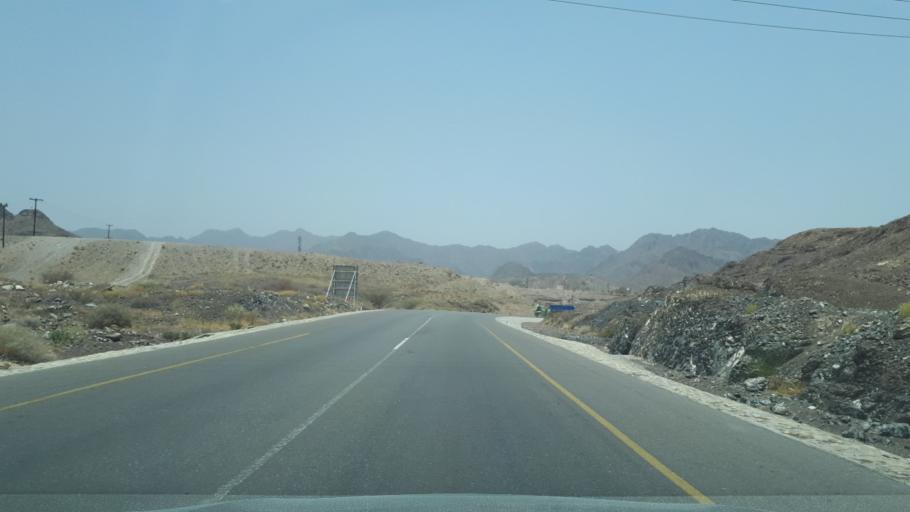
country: OM
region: Al Batinah
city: Rustaq
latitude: 23.4190
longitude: 57.3009
